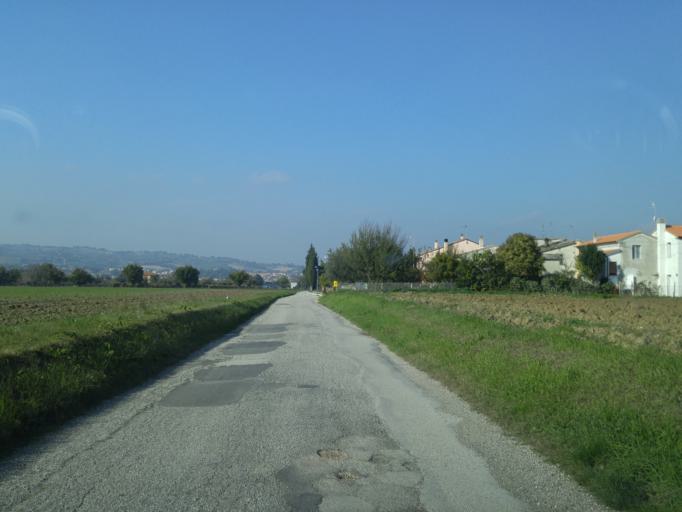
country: IT
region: The Marches
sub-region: Provincia di Pesaro e Urbino
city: Villanova
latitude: 43.7351
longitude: 12.9320
